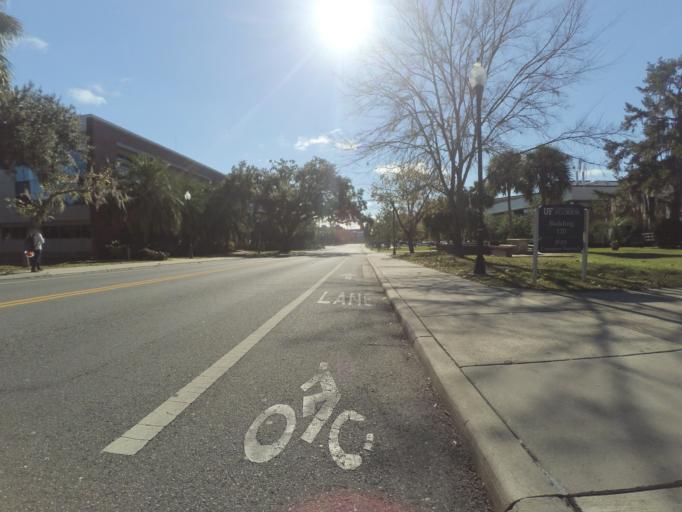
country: US
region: Florida
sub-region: Alachua County
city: Gainesville
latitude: 29.6476
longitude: -82.3435
